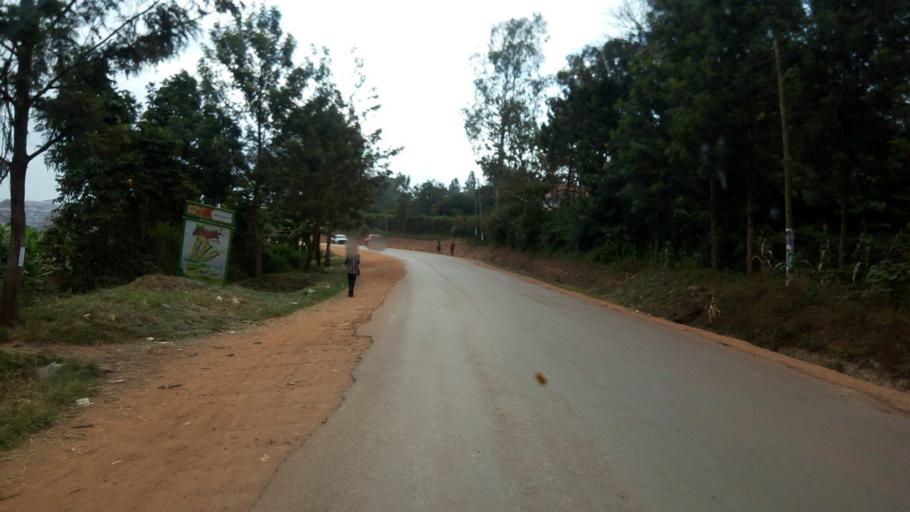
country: UG
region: Western Region
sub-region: Mbarara District
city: Mbarara
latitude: -0.6047
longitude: 30.6542
